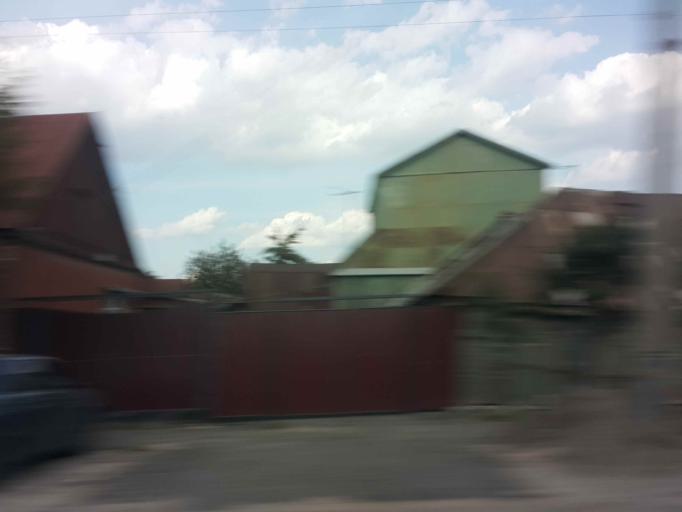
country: RU
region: Tambov
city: Tambov
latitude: 52.7152
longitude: 41.4394
